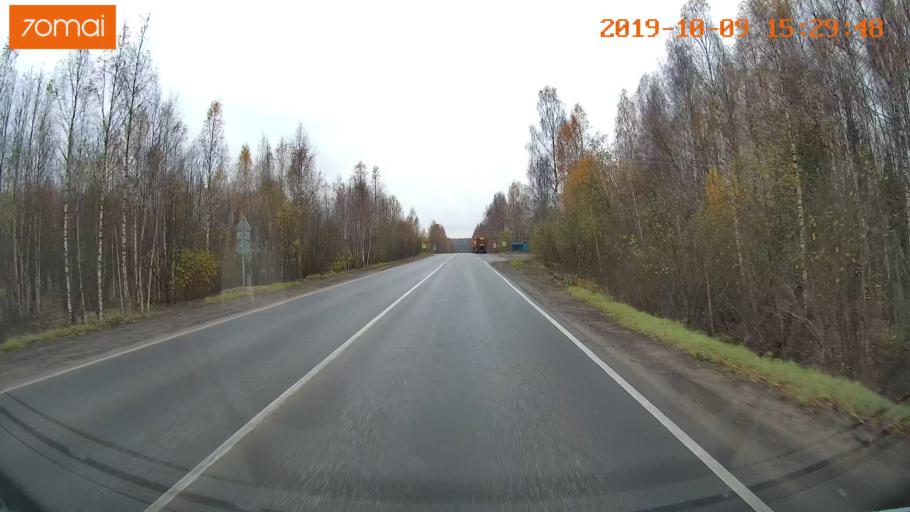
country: RU
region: Kostroma
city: Susanino
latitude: 57.9872
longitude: 41.3365
